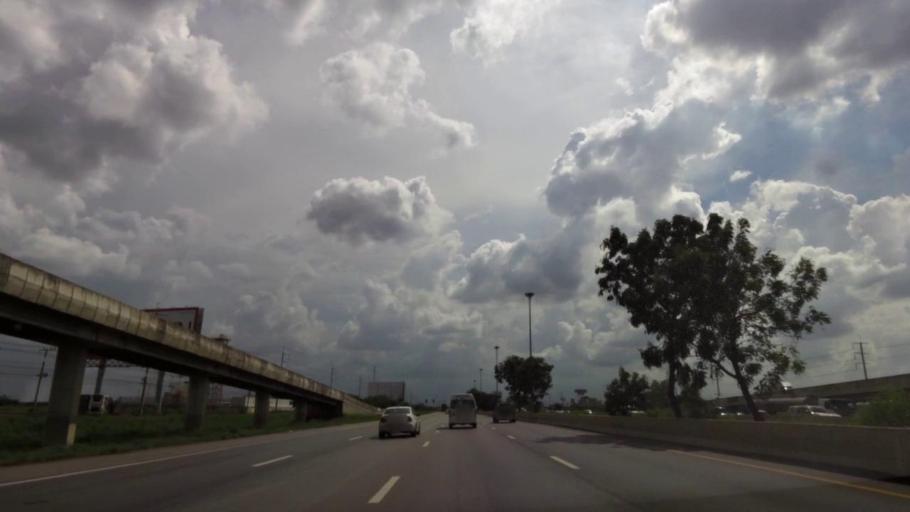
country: TH
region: Phra Nakhon Si Ayutthaya
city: Bang Pa-in
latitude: 14.2561
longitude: 100.6136
